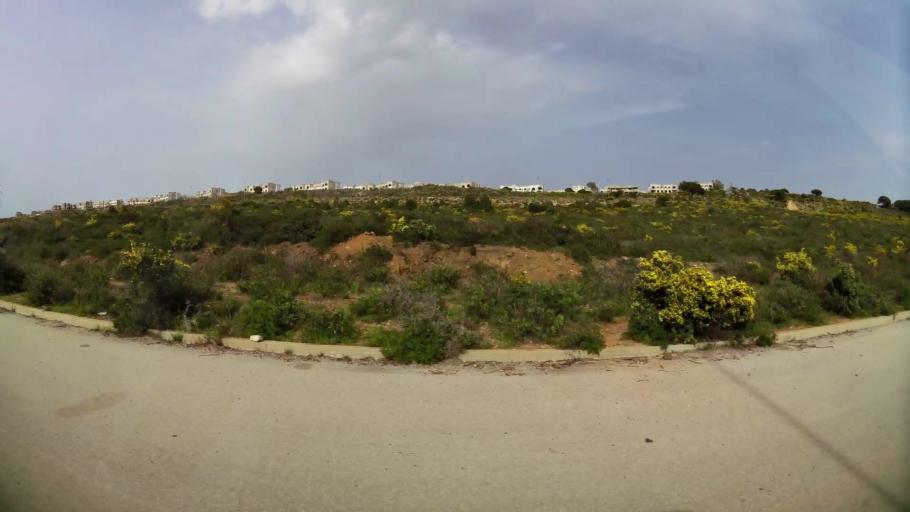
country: MA
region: Tanger-Tetouan
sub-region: Tanger-Assilah
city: Boukhalef
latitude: 35.6926
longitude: -5.9401
